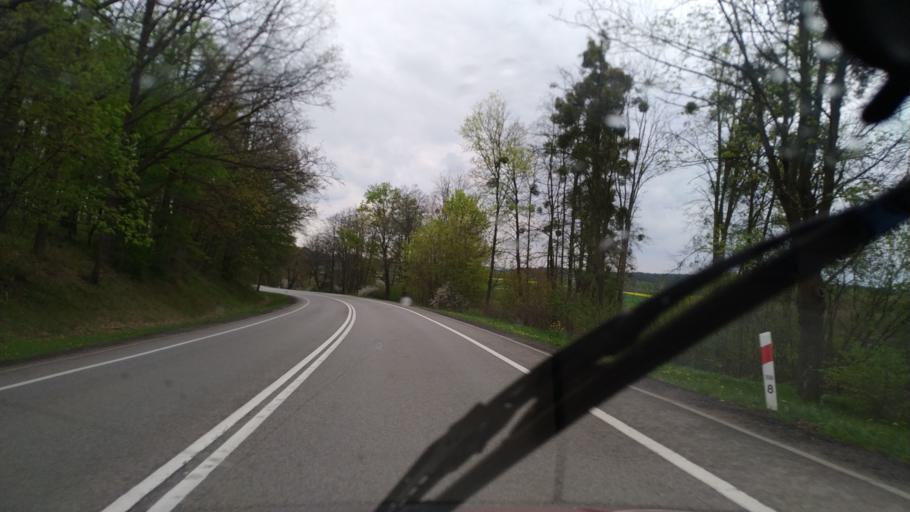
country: PL
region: Pomeranian Voivodeship
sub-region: Powiat tczewski
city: Subkowy
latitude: 54.0442
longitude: 18.7134
